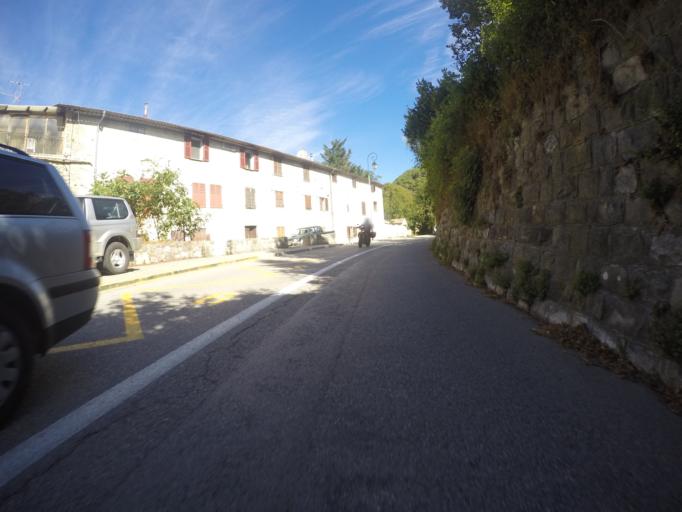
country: FR
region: Provence-Alpes-Cote d'Azur
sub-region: Departement des Alpes-Maritimes
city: Gilette
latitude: 43.9622
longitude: 7.1537
